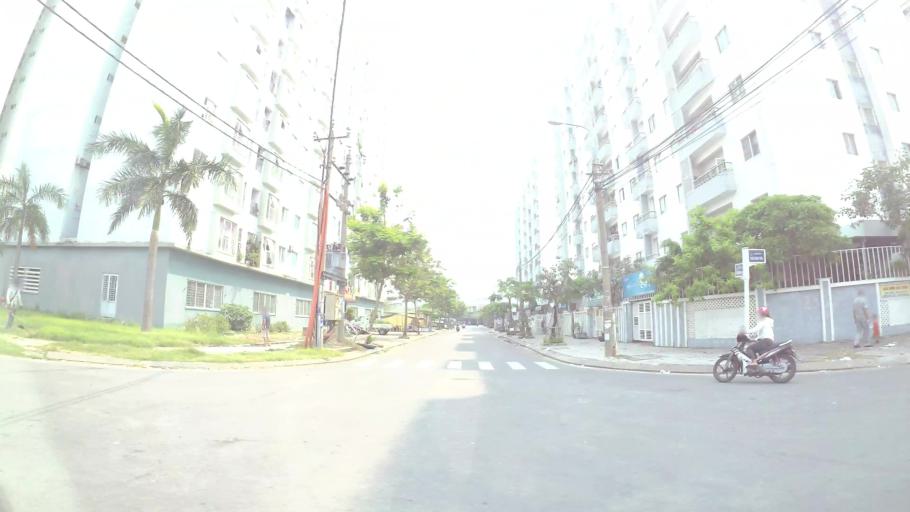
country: VN
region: Da Nang
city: Da Nang
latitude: 16.0894
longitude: 108.2329
